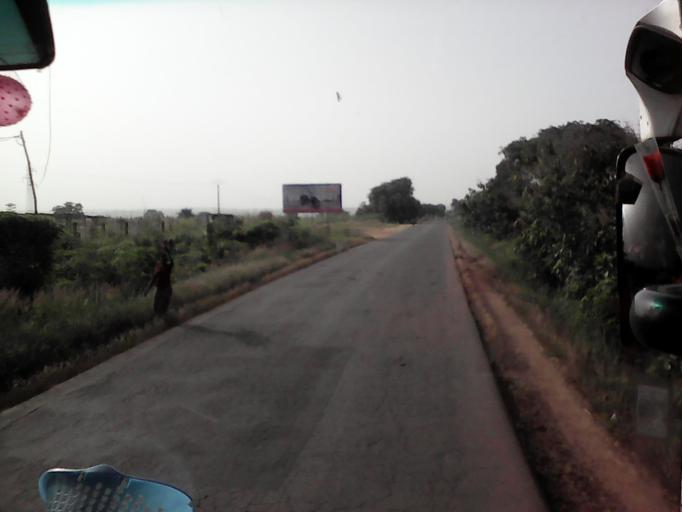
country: TG
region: Kara
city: Kara
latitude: 9.5199
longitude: 1.2086
